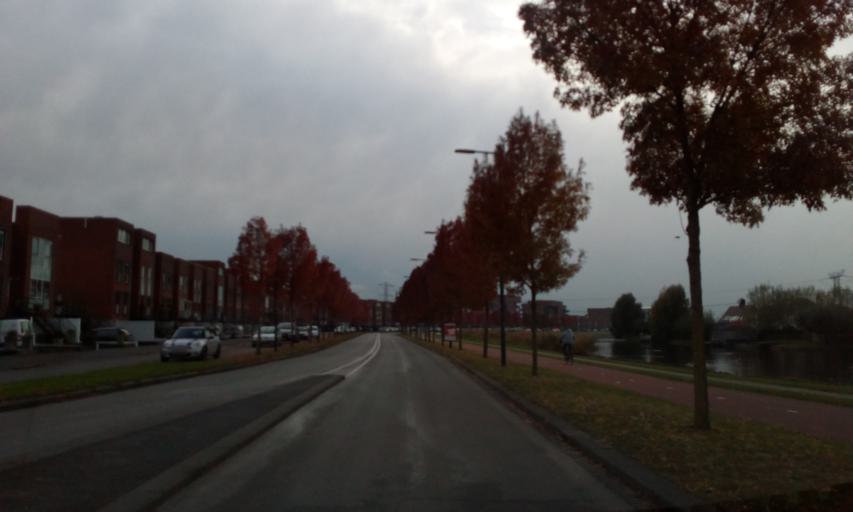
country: NL
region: South Holland
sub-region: Gemeente Capelle aan den IJssel
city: Capelle aan den IJssel
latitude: 51.9876
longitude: 4.5967
